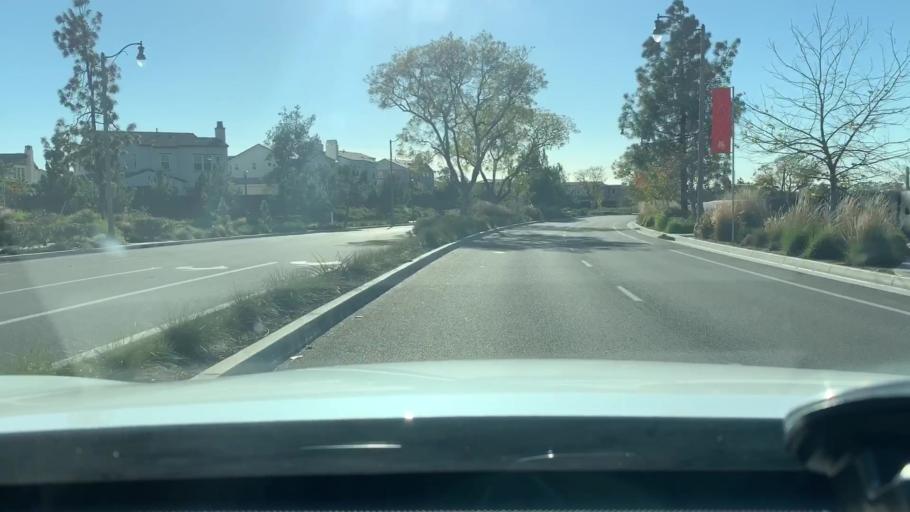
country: US
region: California
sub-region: Orange County
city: Lake Forest
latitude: 33.6932
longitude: -117.7318
